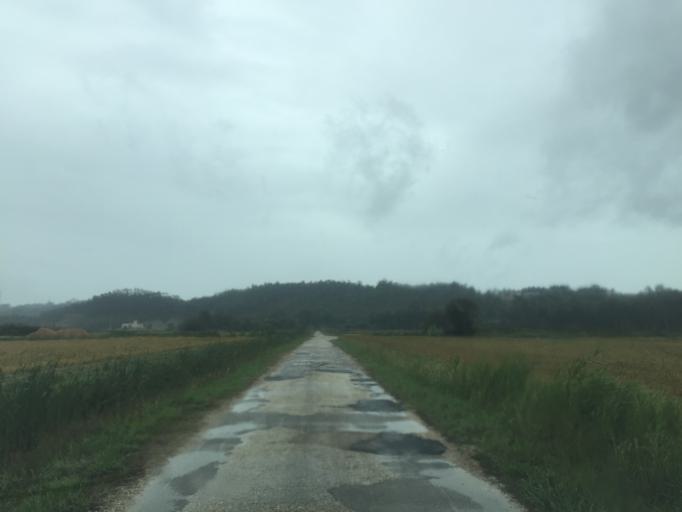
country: PT
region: Coimbra
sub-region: Figueira da Foz
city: Lavos
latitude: 40.0980
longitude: -8.8090
